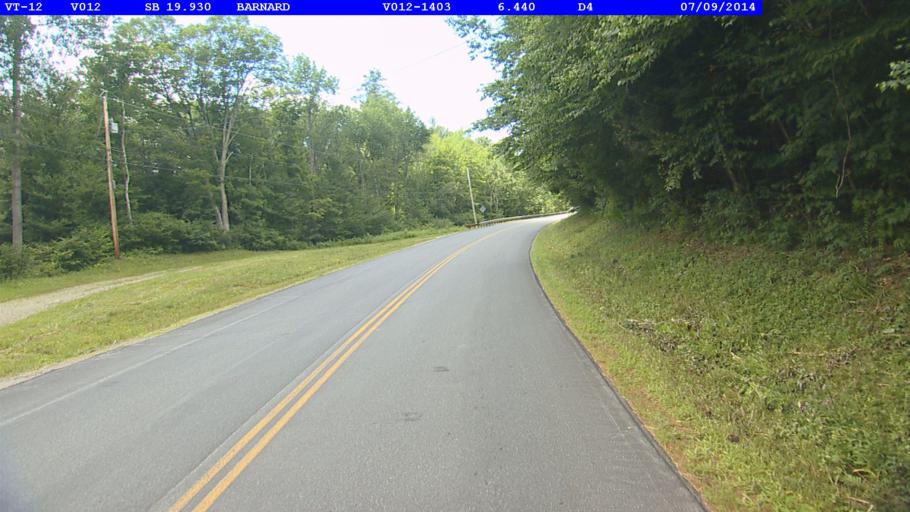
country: US
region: Vermont
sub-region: Windsor County
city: Woodstock
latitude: 43.7496
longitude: -72.6322
